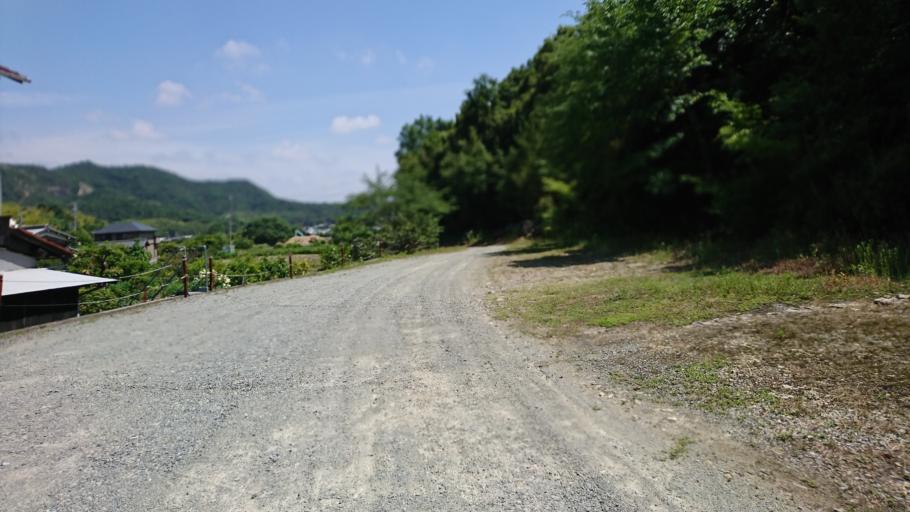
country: JP
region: Hyogo
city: Kakogawacho-honmachi
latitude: 34.8091
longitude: 134.7844
